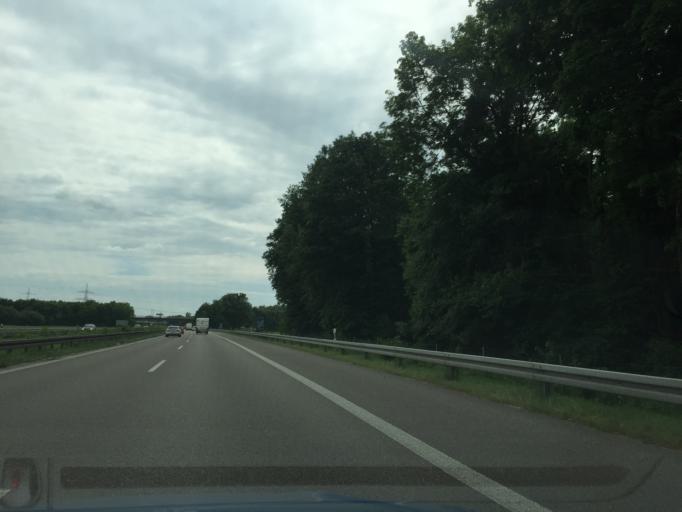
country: DE
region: Bavaria
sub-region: Swabia
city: Senden
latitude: 48.3415
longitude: 10.0259
